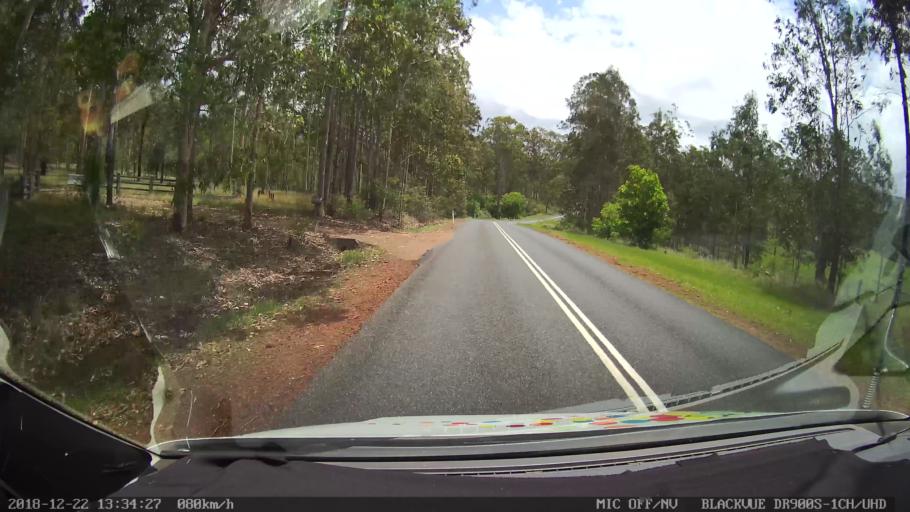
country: AU
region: New South Wales
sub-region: Clarence Valley
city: Coutts Crossing
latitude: -29.8698
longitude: 152.8168
